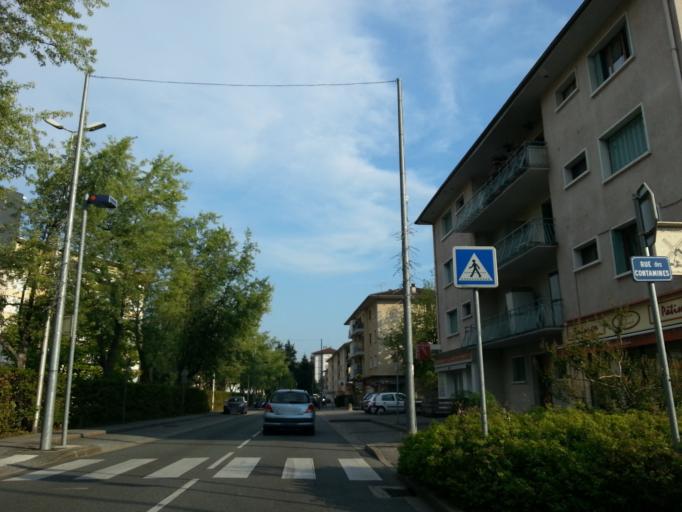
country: FR
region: Rhone-Alpes
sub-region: Departement de la Haute-Savoie
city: Annecy-le-Vieux
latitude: 45.9125
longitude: 6.1436
